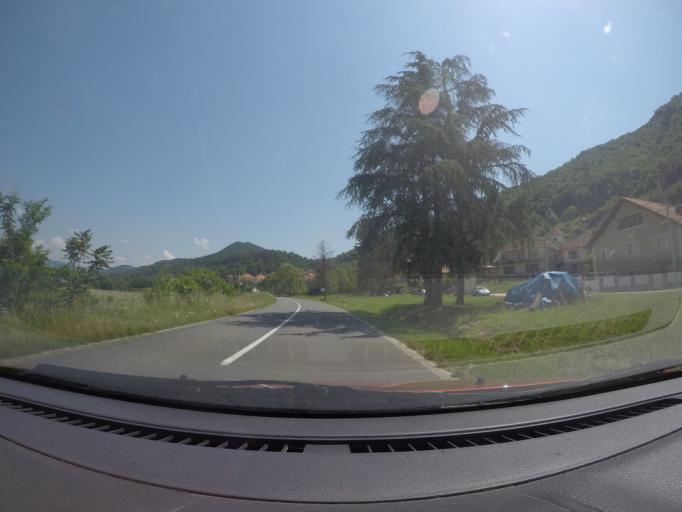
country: RO
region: Mehedinti
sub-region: Municipiul Orsova
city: Orsova
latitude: 44.6851
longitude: 22.4110
